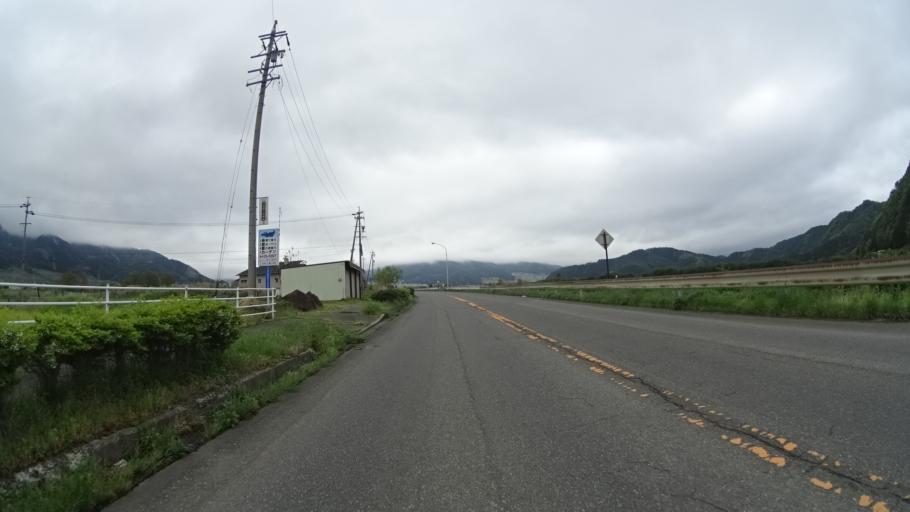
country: JP
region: Nagano
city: Nakano
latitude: 36.7539
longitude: 138.3985
